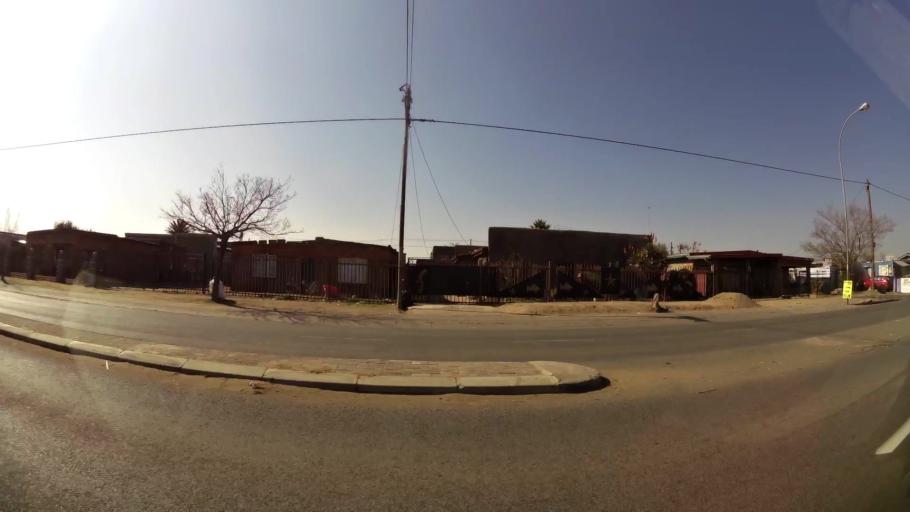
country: ZA
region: Orange Free State
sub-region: Mangaung Metropolitan Municipality
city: Bloemfontein
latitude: -29.1503
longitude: 26.2401
